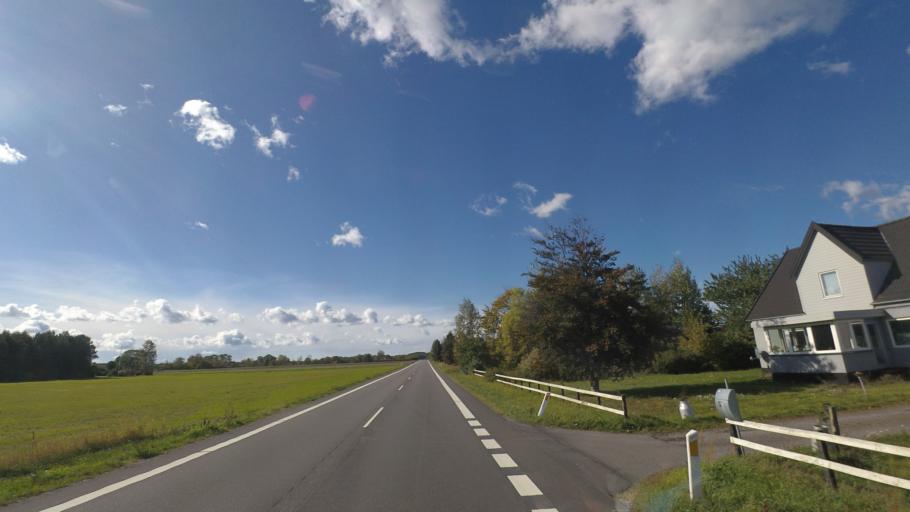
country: DK
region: Capital Region
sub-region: Bornholm Kommune
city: Nexo
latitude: 55.0609
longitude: 15.0587
